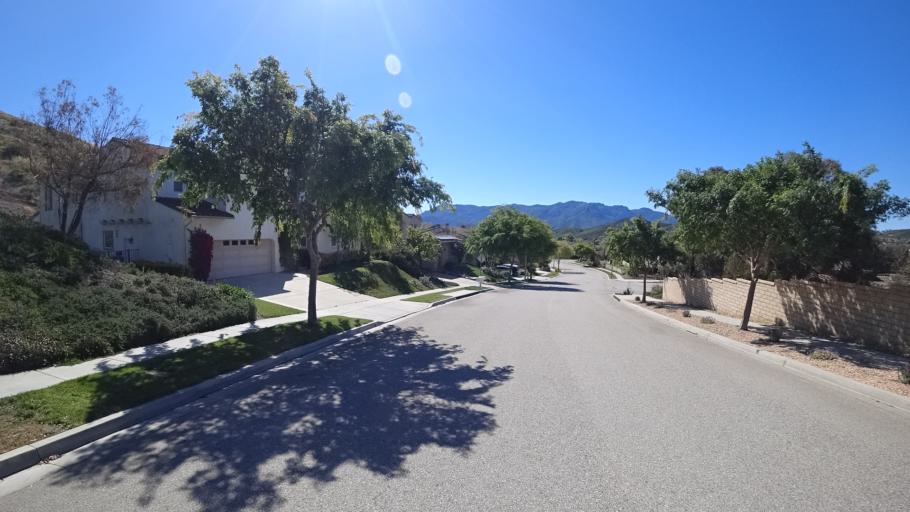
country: US
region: California
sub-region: Ventura County
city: Casa Conejo
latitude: 34.1803
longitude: -118.9825
